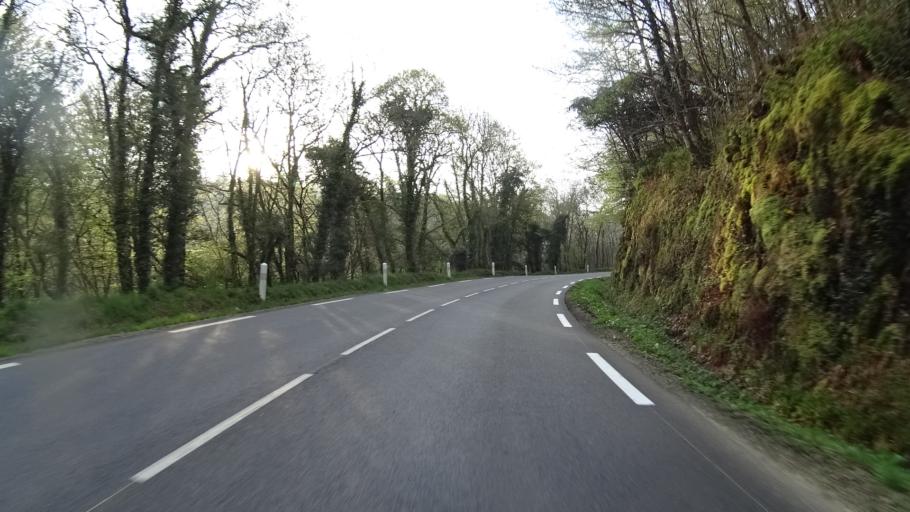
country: FR
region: Brittany
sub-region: Departement du Finistere
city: La Roche-Maurice
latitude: 48.4645
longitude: -4.1978
